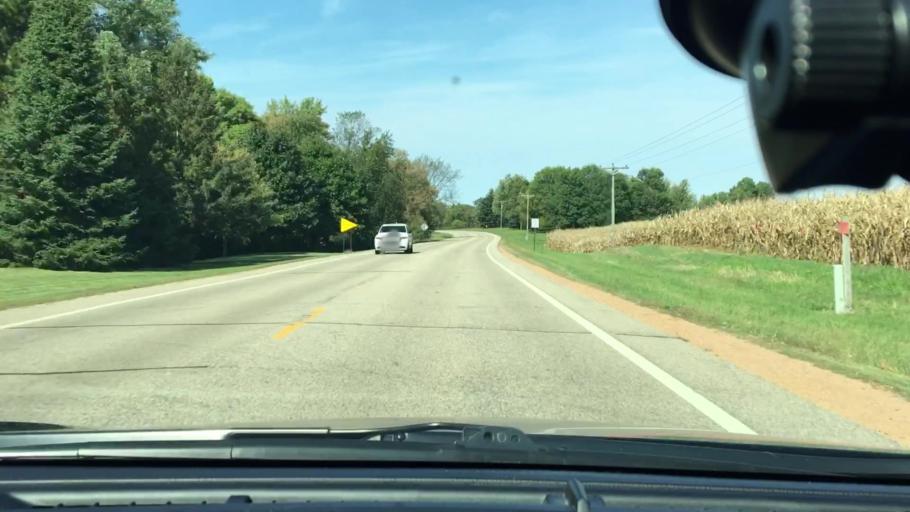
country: US
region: Minnesota
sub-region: Hennepin County
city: Corcoran
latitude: 45.0984
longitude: -93.5524
